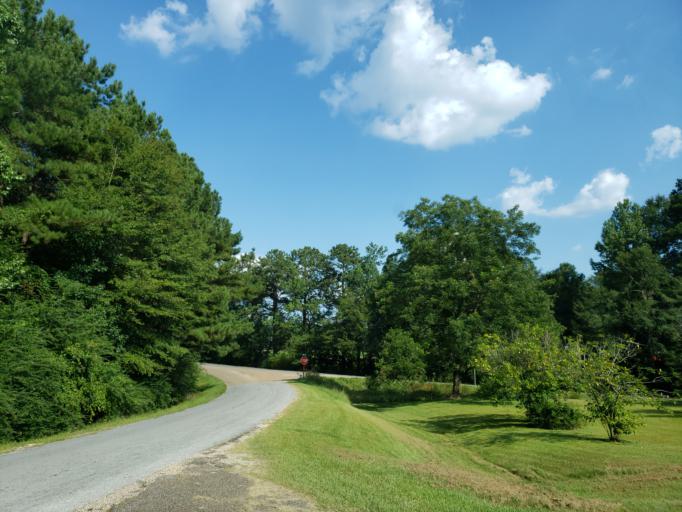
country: US
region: Mississippi
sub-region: Jones County
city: Sharon
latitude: 31.9202
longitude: -89.0391
